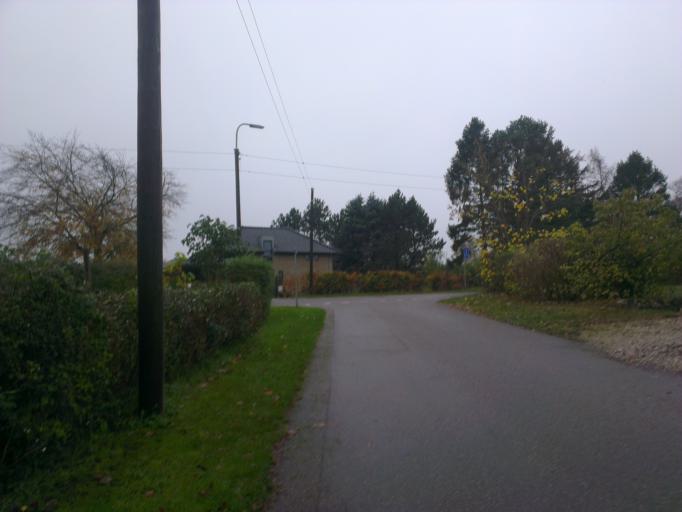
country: DK
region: Capital Region
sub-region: Frederikssund Kommune
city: Jaegerspris
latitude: 55.8535
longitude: 11.9884
